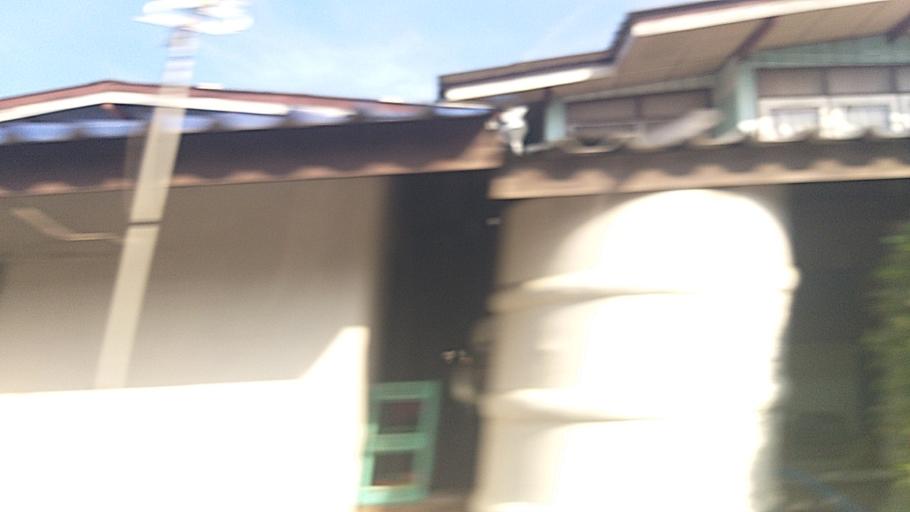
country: TH
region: Pathum Thani
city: Thanyaburi
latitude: 13.9891
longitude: 100.7300
